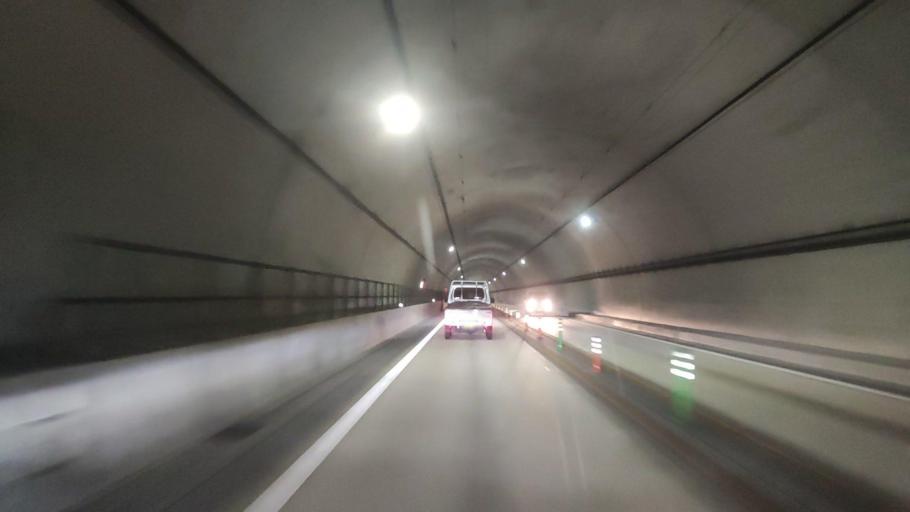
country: JP
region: Wakayama
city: Tanabe
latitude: 33.6078
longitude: 135.4277
